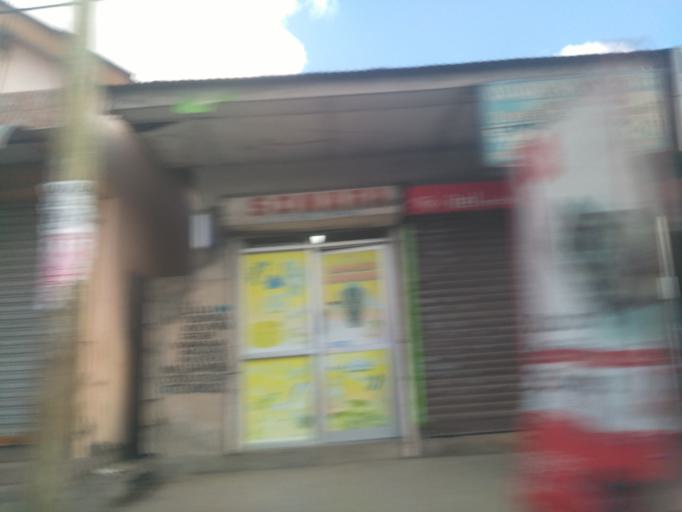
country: TZ
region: Dar es Salaam
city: Dar es Salaam
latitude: -6.8691
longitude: 39.2592
